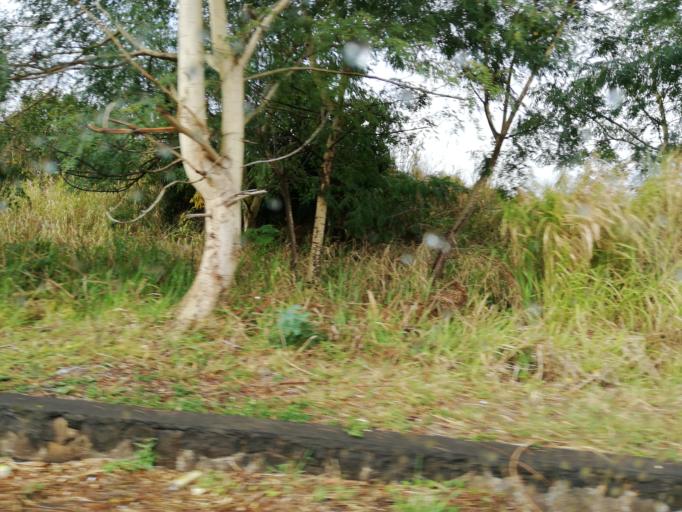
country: MU
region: Pamplemousses
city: Long Mountain
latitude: -20.1248
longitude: 57.5686
